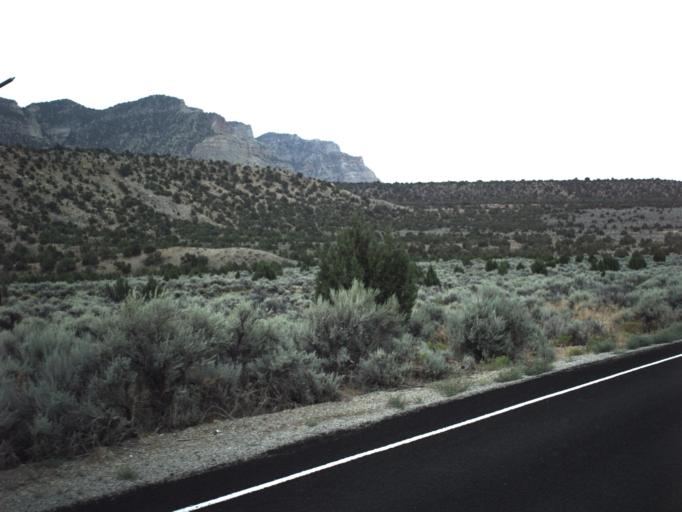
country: US
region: Utah
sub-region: Carbon County
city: East Carbon City
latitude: 39.5132
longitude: -110.3934
